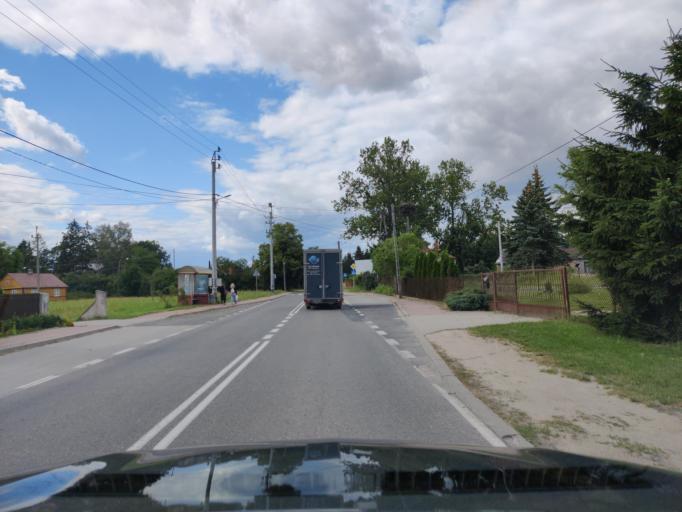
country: PL
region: Masovian Voivodeship
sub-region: Powiat sokolowski
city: Kosow Lacki
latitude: 52.5872
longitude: 22.1525
